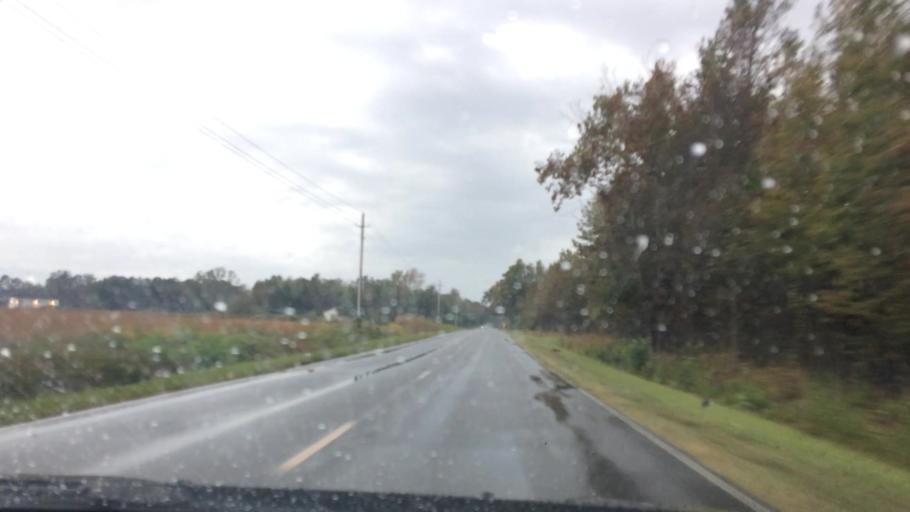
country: US
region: North Carolina
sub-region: Pitt County
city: Grifton
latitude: 35.4029
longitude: -77.4153
